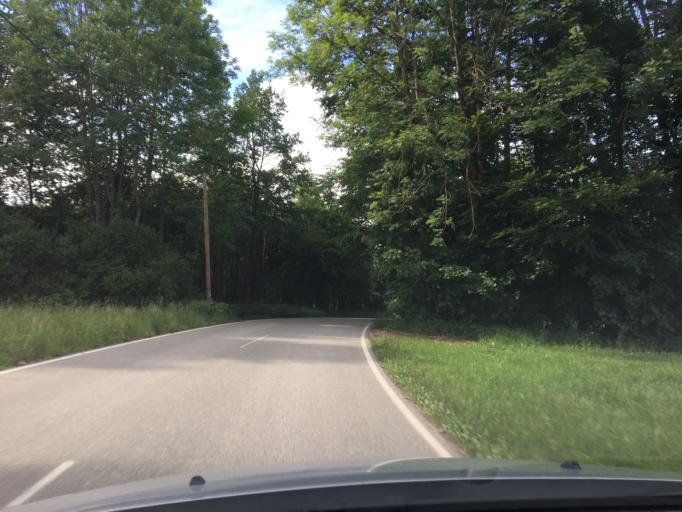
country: DE
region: Bavaria
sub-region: Upper Bavaria
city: Niedertaufkirchen
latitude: 48.3697
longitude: 12.5704
